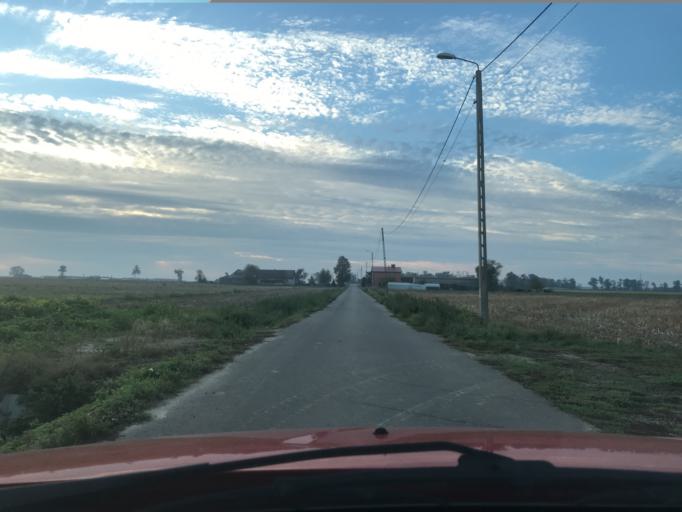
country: PL
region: Greater Poland Voivodeship
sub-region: Powiat ostrowski
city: Skalmierzyce
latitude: 51.7624
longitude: 17.8977
